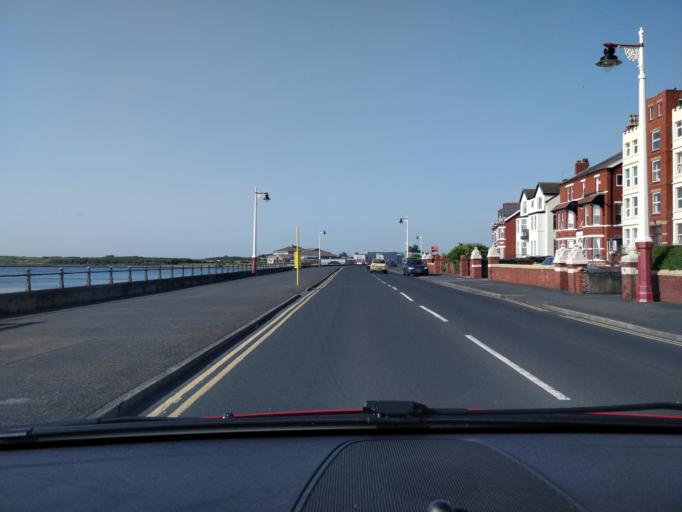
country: GB
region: England
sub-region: Sefton
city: Southport
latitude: 53.6577
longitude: -3.0008
